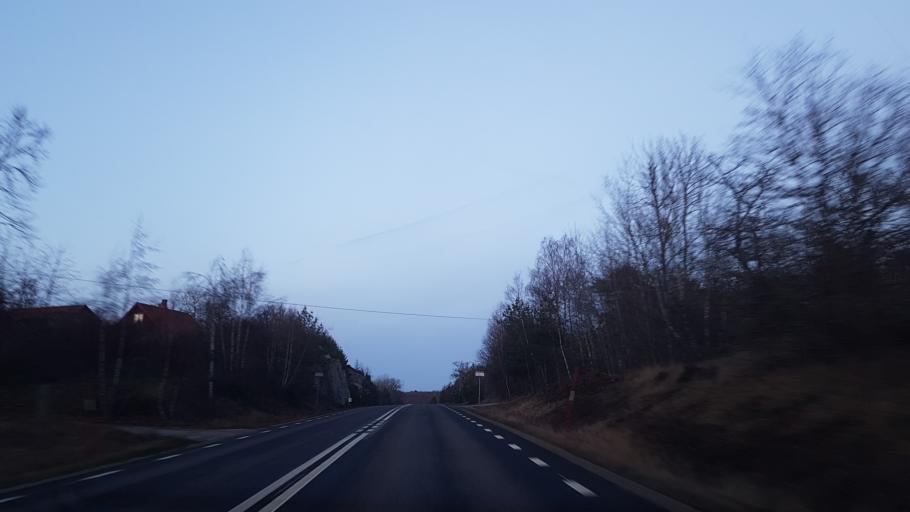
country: SE
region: Blekinge
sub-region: Karlskrona Kommun
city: Jaemjoe
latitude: 56.1629
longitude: 15.8298
